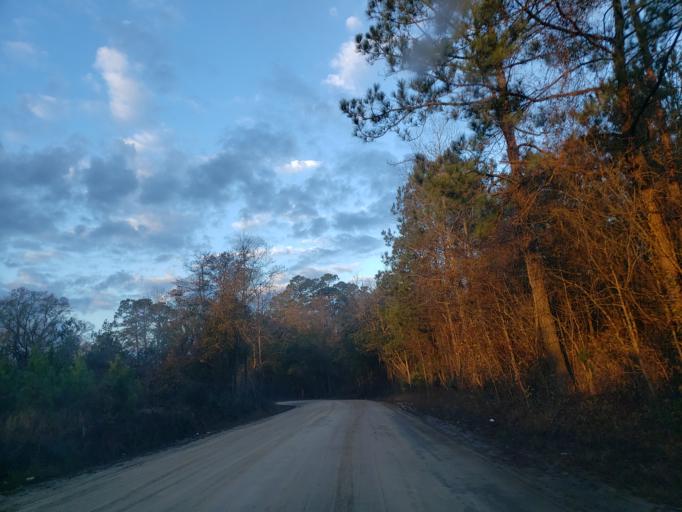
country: US
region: Georgia
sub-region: Chatham County
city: Bloomingdale
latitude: 32.1267
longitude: -81.3232
